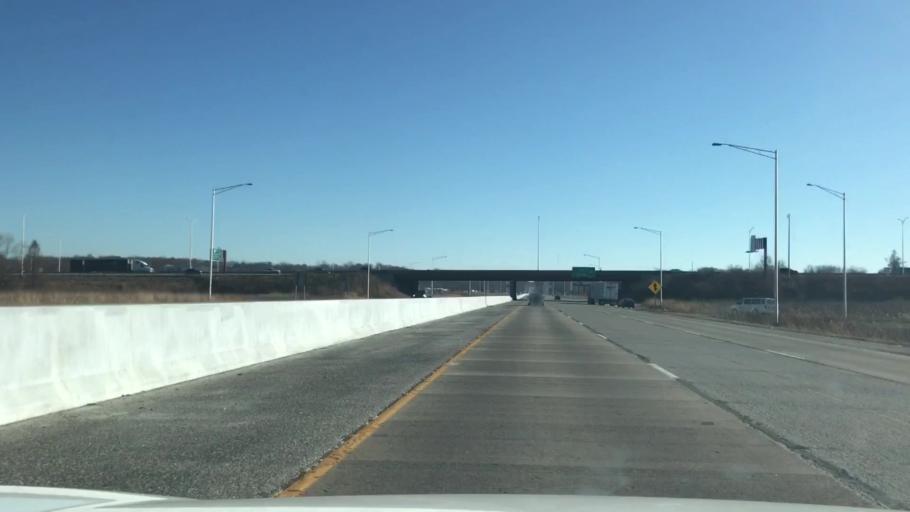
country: US
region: Illinois
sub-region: Saint Clair County
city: Alorton
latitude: 38.5840
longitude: -90.1096
